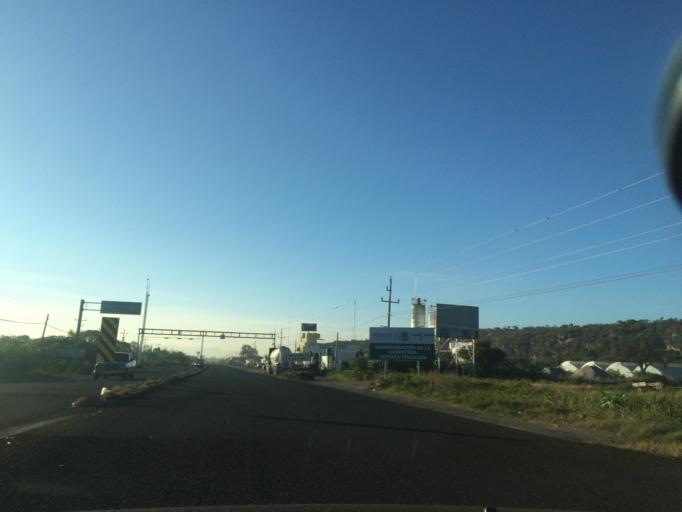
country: MX
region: Puebla
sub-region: Santiago Miahuatlan
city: San Jose Monte Chiquito
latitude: 18.4850
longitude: -97.4526
